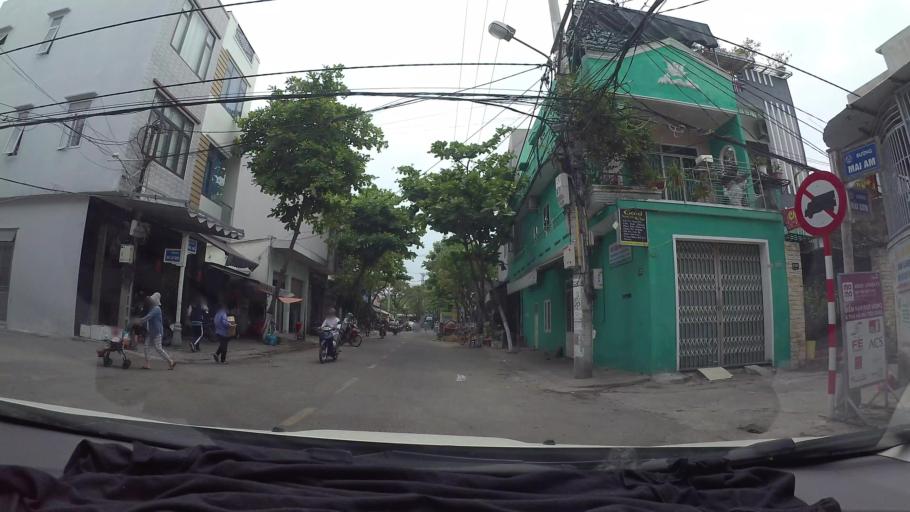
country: VN
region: Da Nang
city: Da Nang
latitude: 16.0834
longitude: 108.2164
